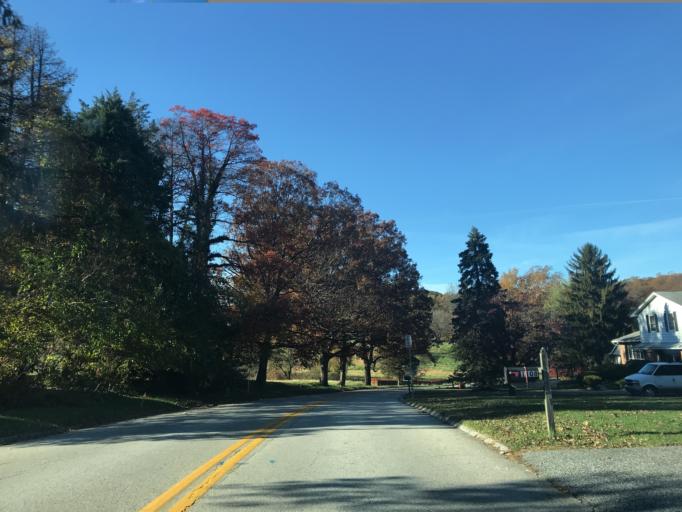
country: US
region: Maryland
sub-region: Baltimore County
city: Hampton
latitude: 39.4092
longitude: -76.5697
